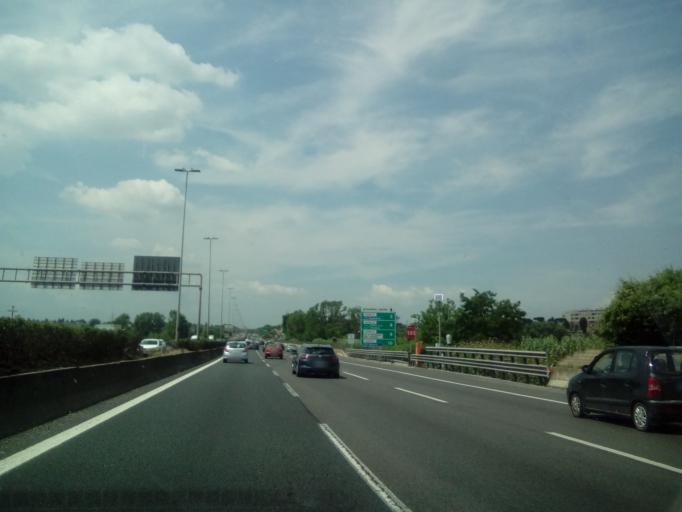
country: IT
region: Latium
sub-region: Citta metropolitana di Roma Capitale
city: Colle Verde
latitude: 41.9361
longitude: 12.5992
